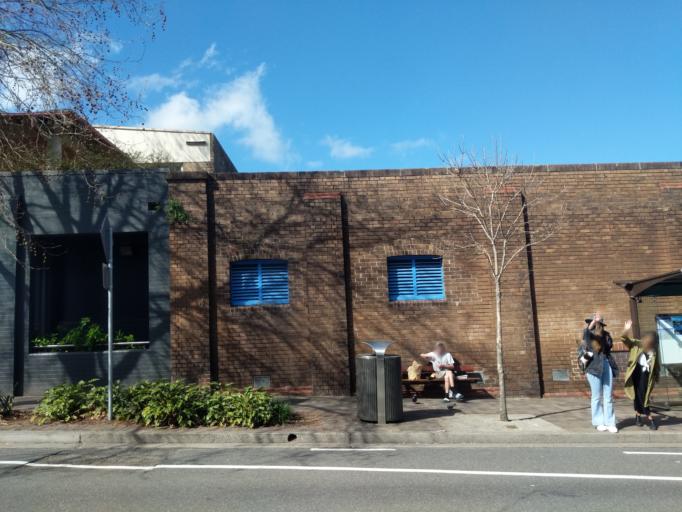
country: AU
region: New South Wales
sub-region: City of Sydney
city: Redfern
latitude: -33.8921
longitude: 151.2125
